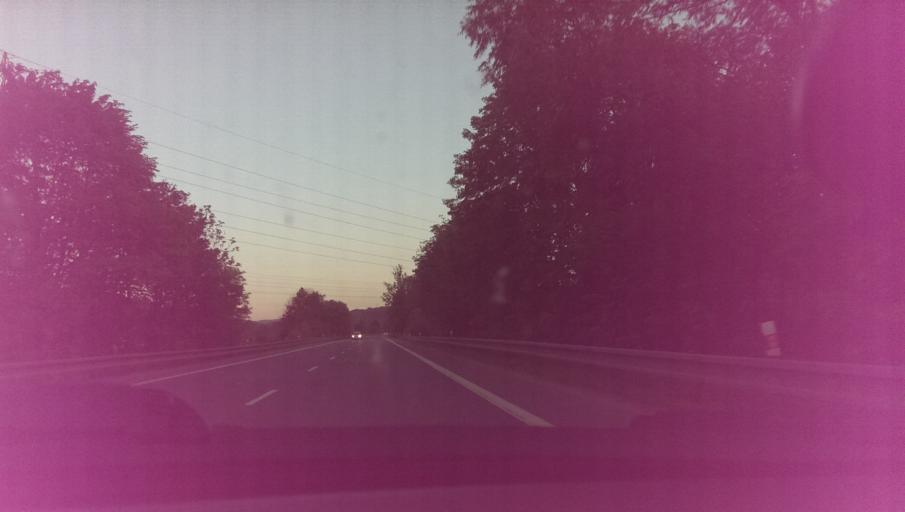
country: CZ
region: Zlin
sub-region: Okres Vsetin
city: Vsetin
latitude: 49.3550
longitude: 17.9678
